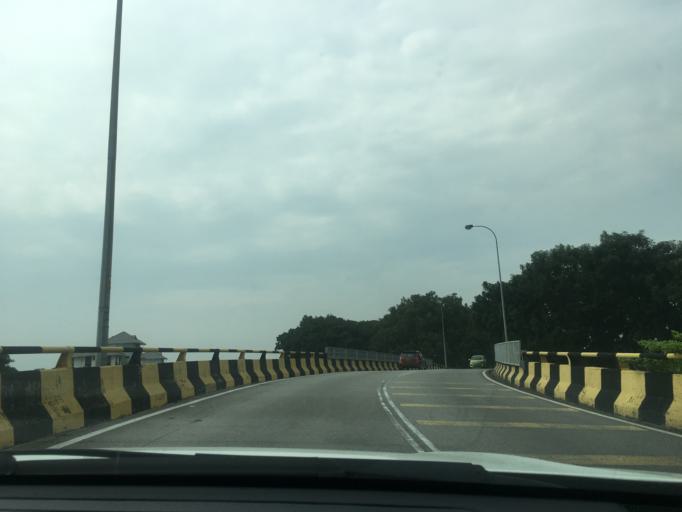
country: MY
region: Selangor
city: Klang
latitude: 3.0464
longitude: 101.4433
